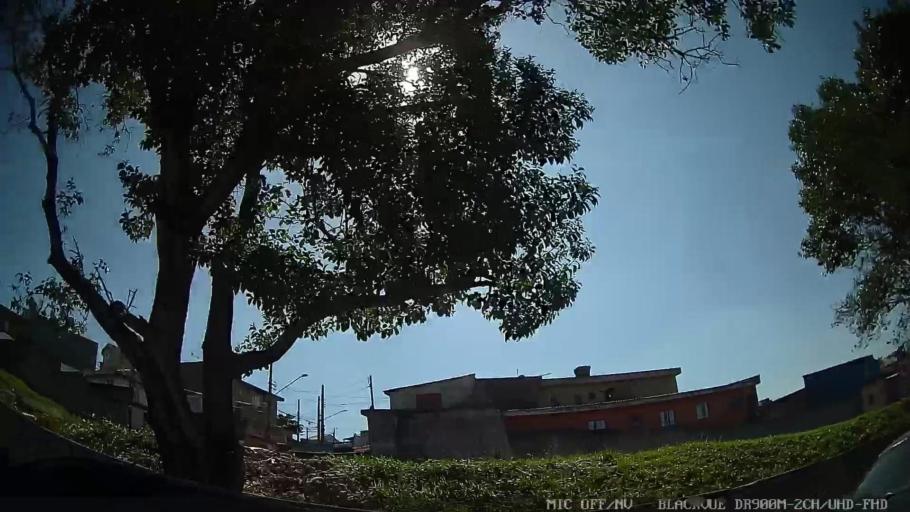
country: BR
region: Sao Paulo
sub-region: Sao Caetano Do Sul
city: Sao Caetano do Sul
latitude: -23.5961
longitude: -46.4953
